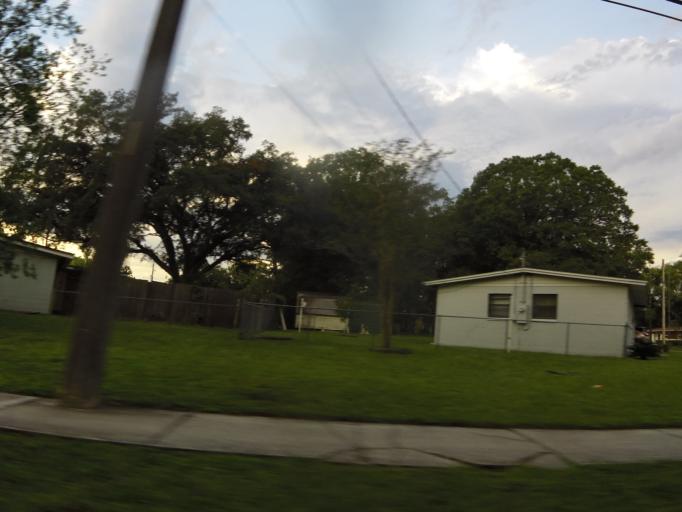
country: US
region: Florida
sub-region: Clay County
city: Bellair-Meadowbrook Terrace
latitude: 30.2718
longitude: -81.7814
